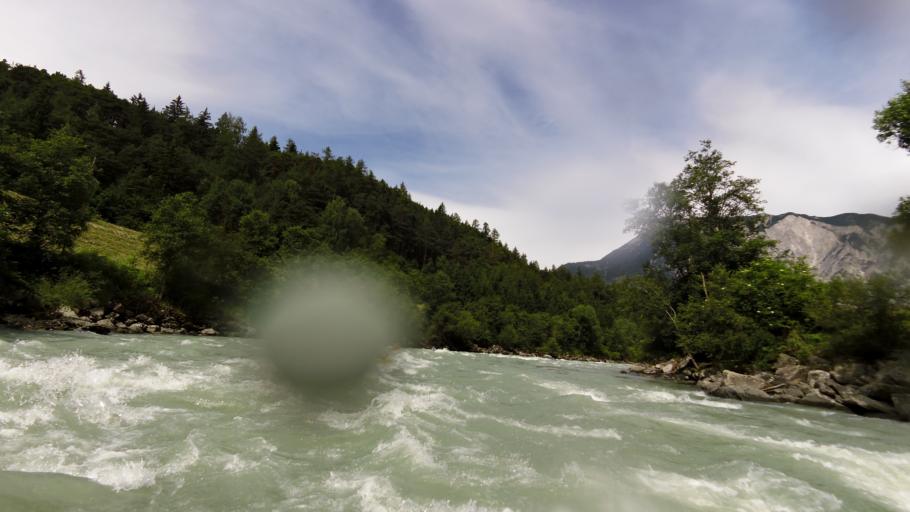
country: AT
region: Tyrol
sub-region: Politischer Bezirk Imst
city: Sautens
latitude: 47.2163
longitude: 10.8604
